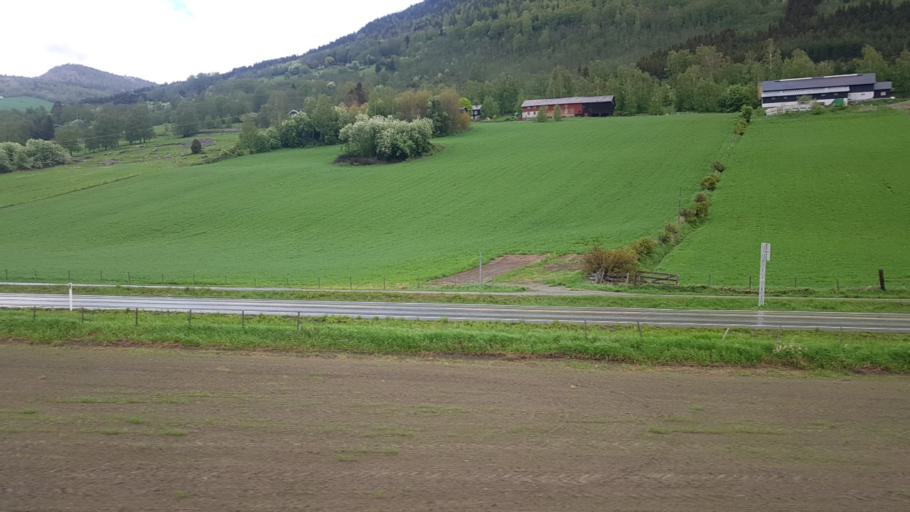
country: NO
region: Oppland
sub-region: Nord-Fron
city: Vinstra
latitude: 61.6639
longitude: 9.6823
